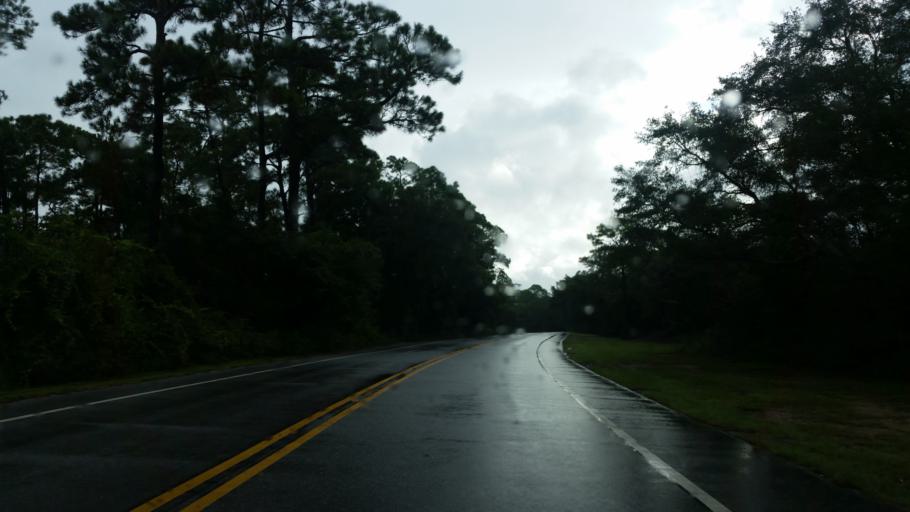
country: US
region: Alabama
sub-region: Baldwin County
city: Gulf Shores
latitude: 30.2617
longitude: -87.6806
